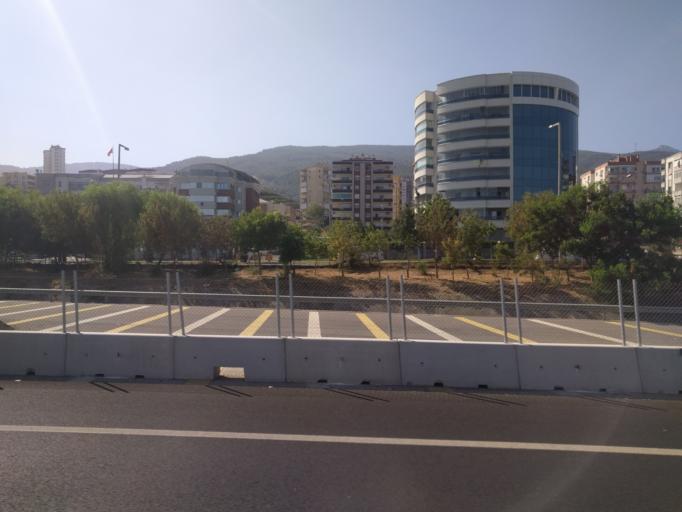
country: TR
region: Izmir
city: Karsiyaka
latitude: 38.3968
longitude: 26.9921
